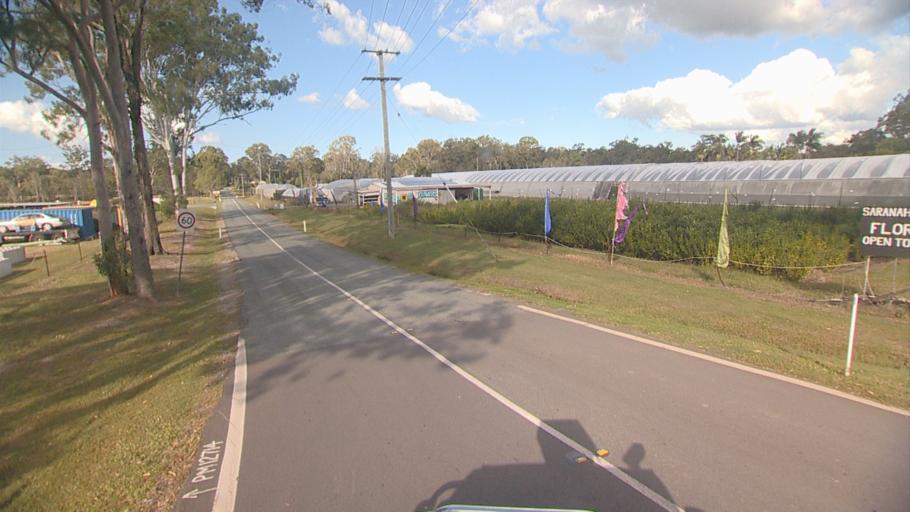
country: AU
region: Queensland
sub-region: Gold Coast
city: Yatala
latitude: -27.6665
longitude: 153.2318
